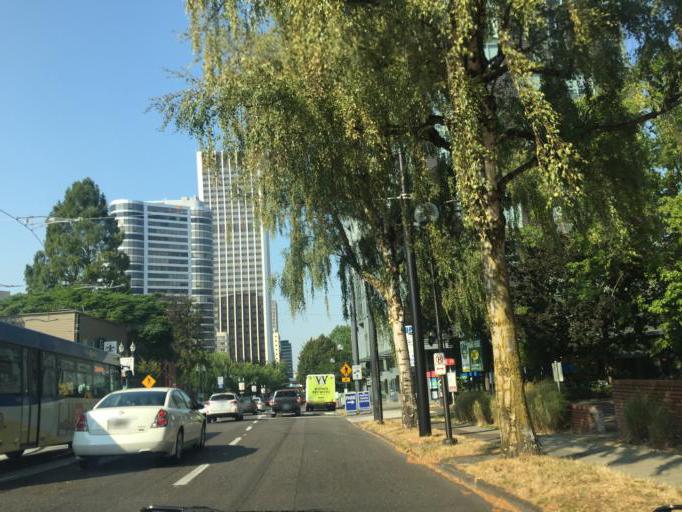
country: US
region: Oregon
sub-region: Multnomah County
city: Portland
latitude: 45.5109
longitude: -122.6807
